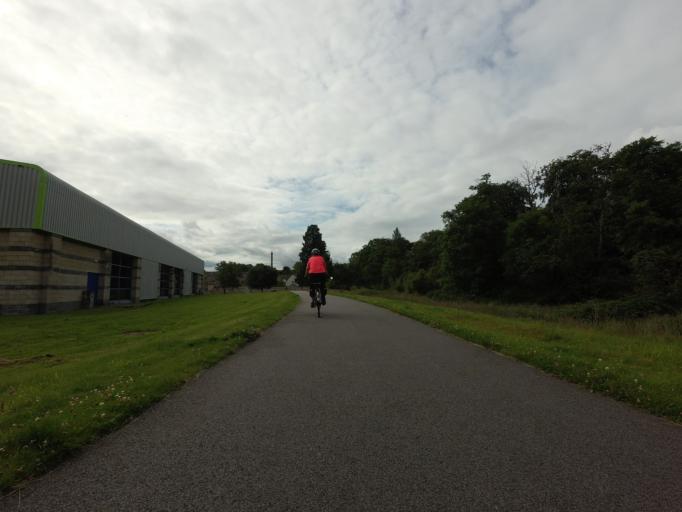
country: GB
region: Scotland
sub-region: Moray
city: Elgin
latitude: 57.6519
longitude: -3.3252
